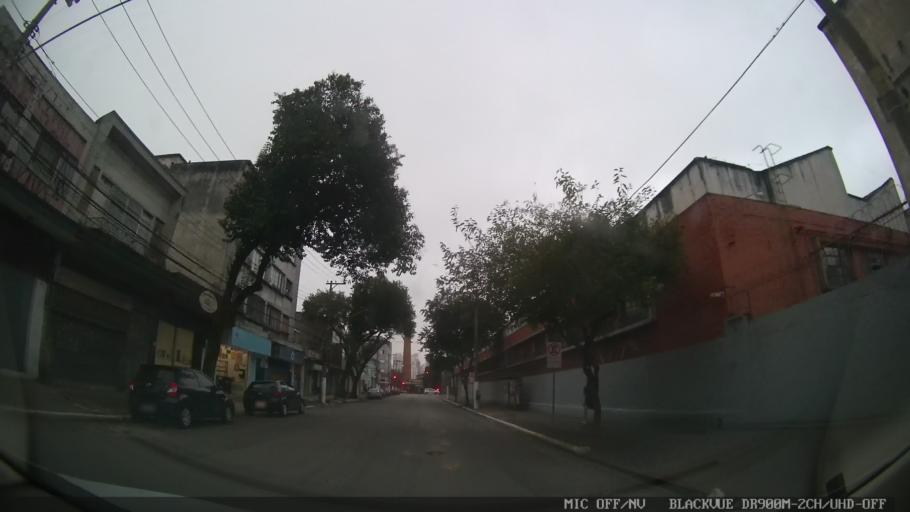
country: BR
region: Sao Paulo
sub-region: Sao Paulo
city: Sao Paulo
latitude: -23.5797
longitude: -46.6035
